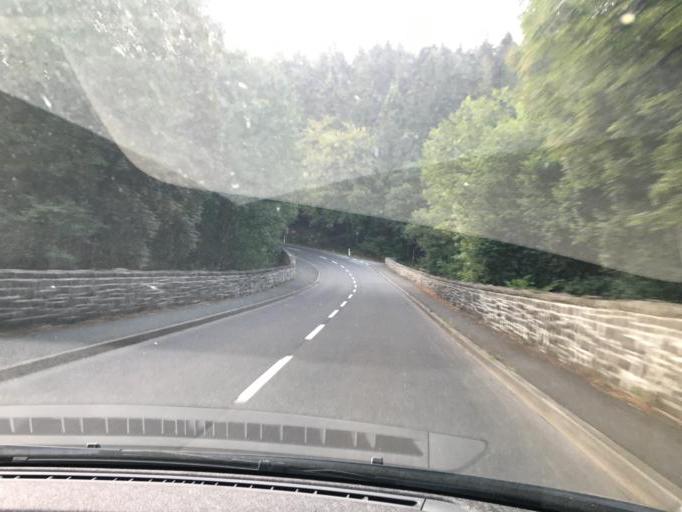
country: DE
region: North Rhine-Westphalia
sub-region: Regierungsbezirk Koln
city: Simmerath
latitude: 50.6567
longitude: 6.3262
